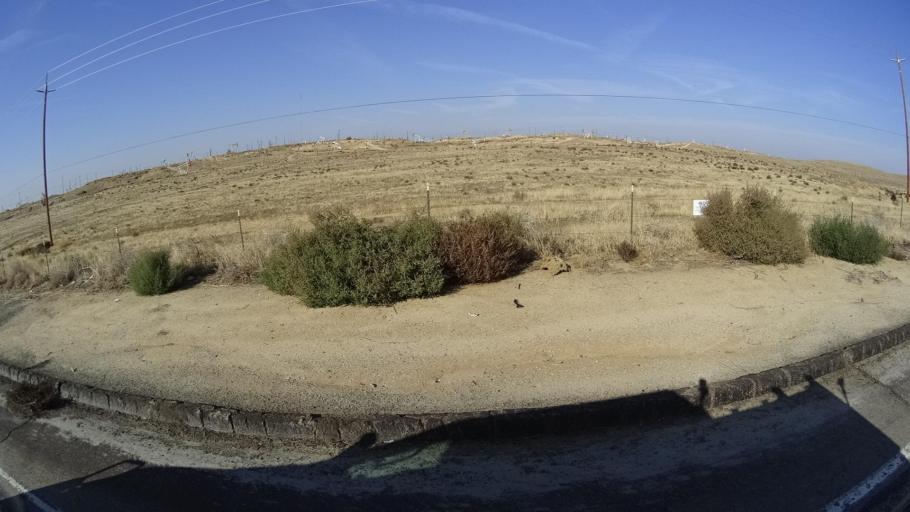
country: US
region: California
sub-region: Kern County
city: Oildale
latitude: 35.4722
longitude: -119.0225
